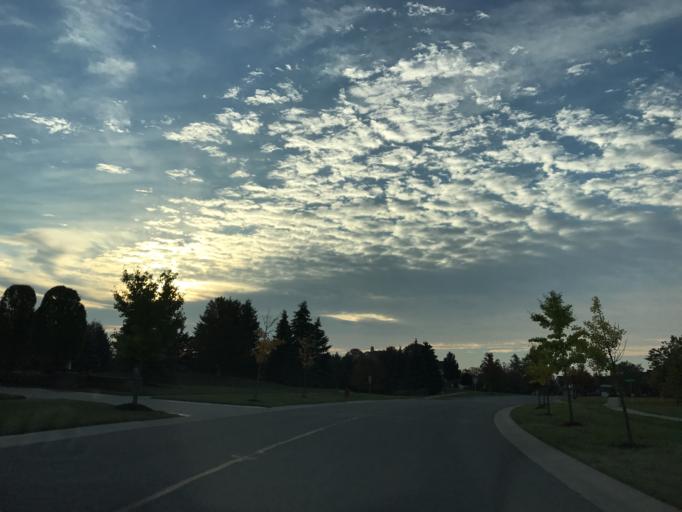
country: US
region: Michigan
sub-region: Oakland County
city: Wixom
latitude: 42.4722
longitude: -83.5465
